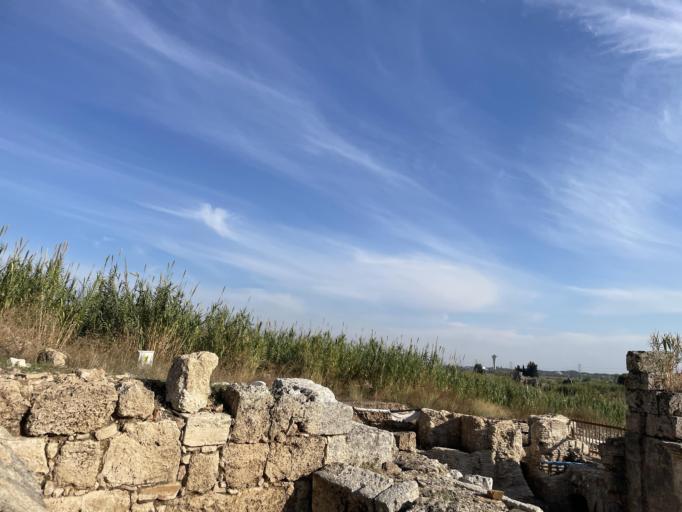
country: TR
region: Antalya
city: Aksu
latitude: 36.9661
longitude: 30.8551
